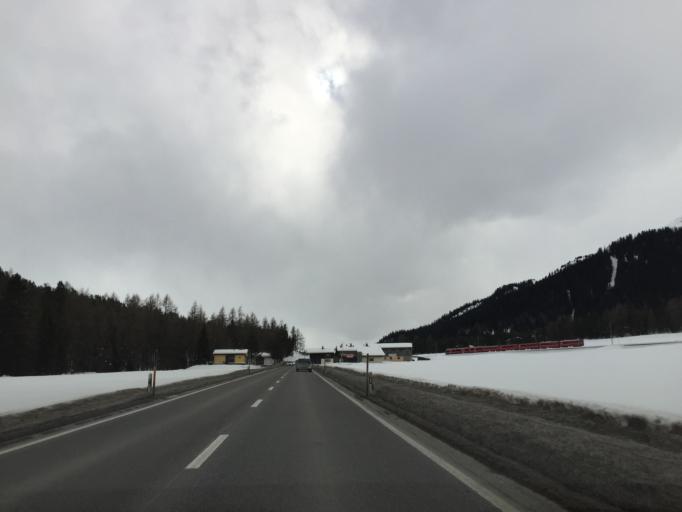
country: CH
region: Grisons
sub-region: Praettigau/Davos District
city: Davos
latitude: 46.8394
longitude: 9.8579
